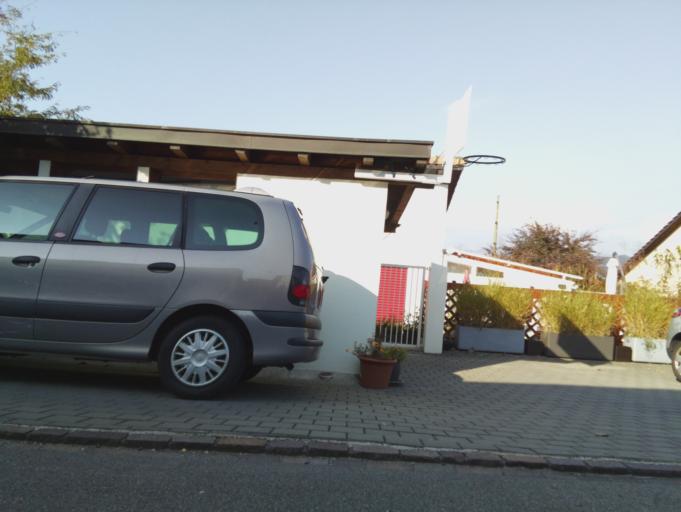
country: CH
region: Schwyz
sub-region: Bezirk March
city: Lachen
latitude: 47.1734
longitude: 8.8785
